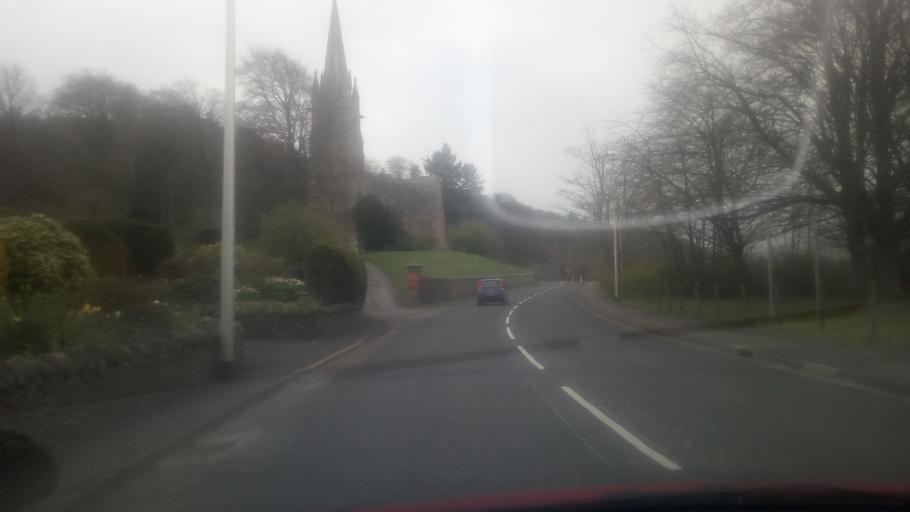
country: GB
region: Scotland
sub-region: The Scottish Borders
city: Galashiels
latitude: 55.6909
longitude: -2.8621
